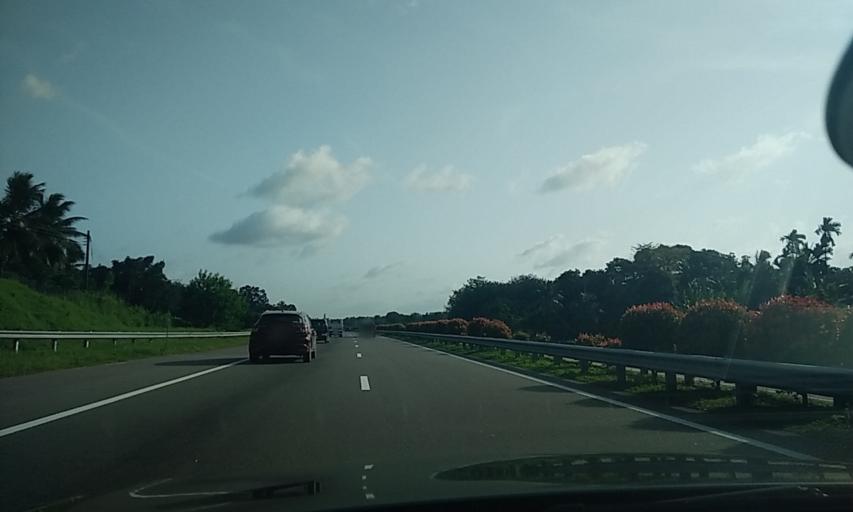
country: LK
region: Western
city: Homagama
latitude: 6.8645
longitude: 79.9782
